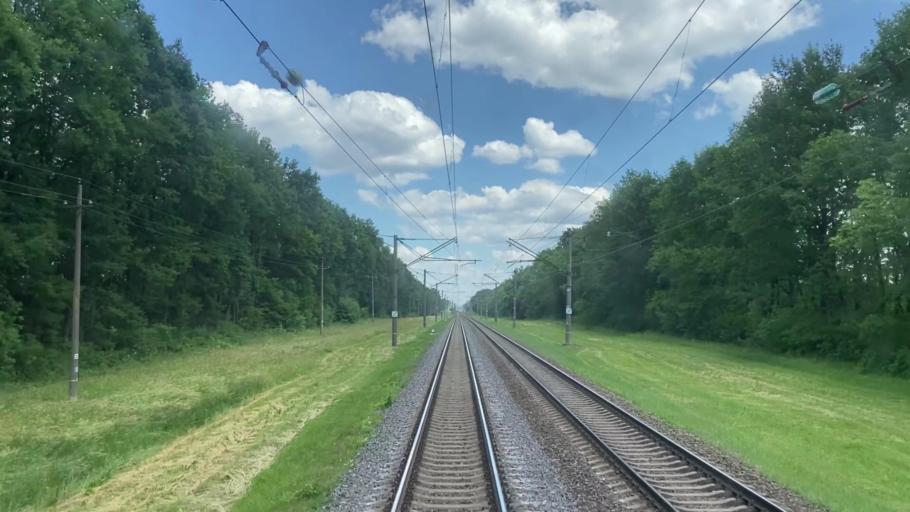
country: BY
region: Brest
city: Byaroza
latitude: 52.5421
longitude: 24.9444
